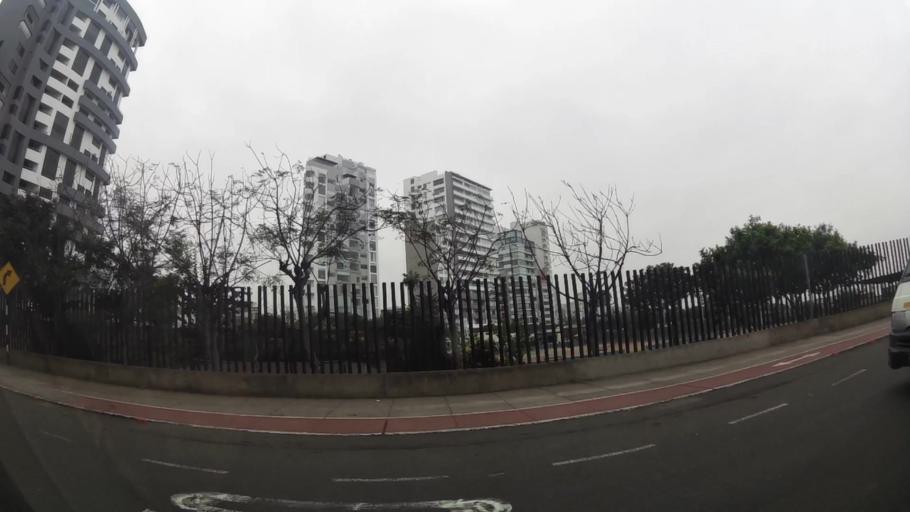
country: PE
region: Lima
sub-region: Lima
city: San Isidro
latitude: -12.1220
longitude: -77.0416
